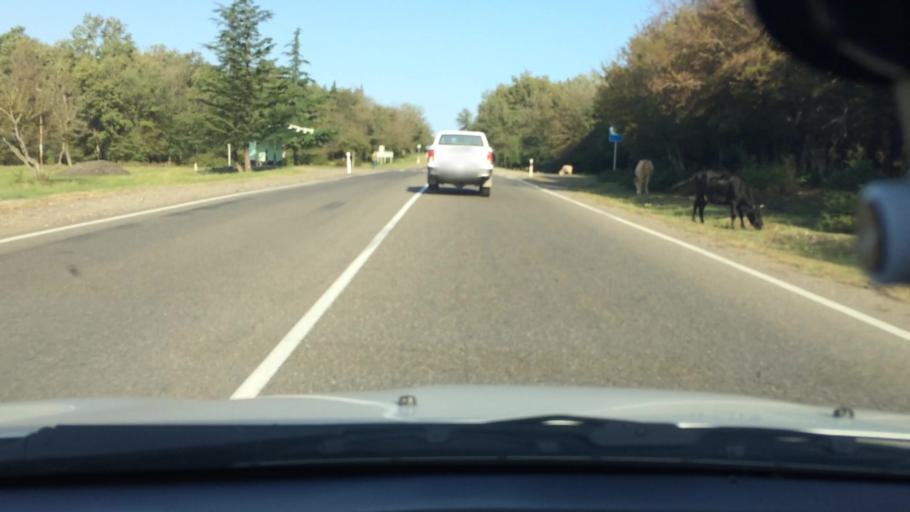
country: GE
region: Imereti
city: Kutaisi
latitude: 42.2325
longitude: 42.7753
